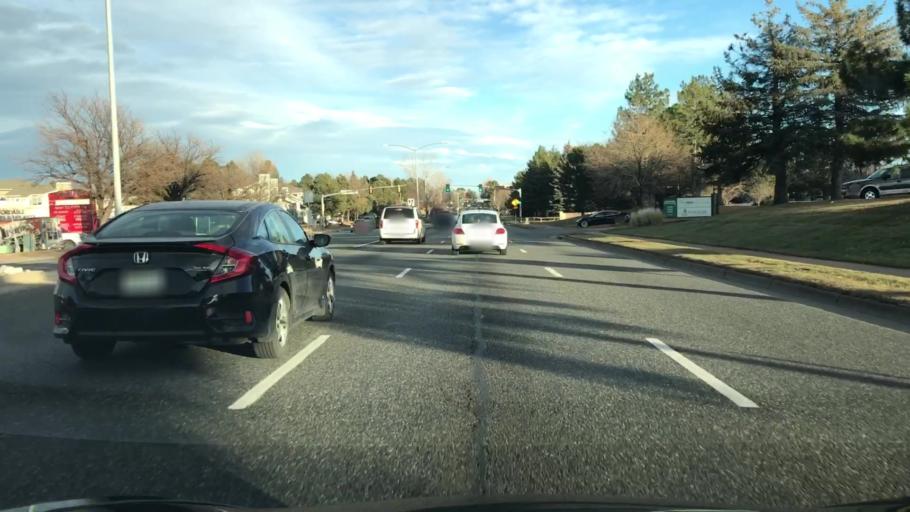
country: US
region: Colorado
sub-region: Adams County
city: Aurora
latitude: 39.6748
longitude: -104.8459
